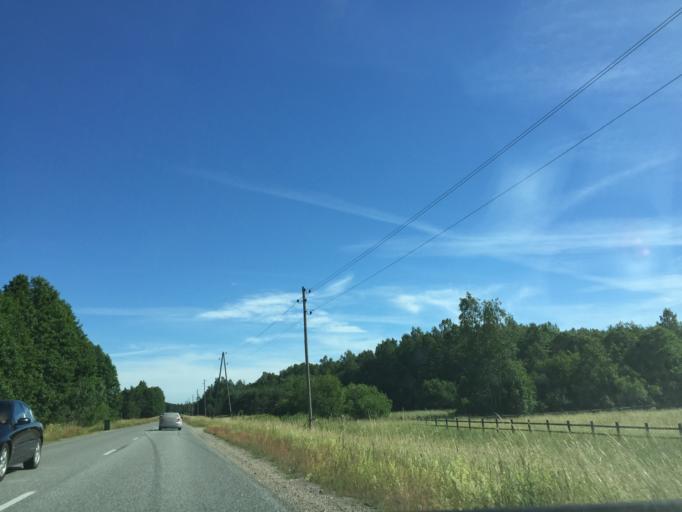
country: LV
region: Rojas
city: Roja
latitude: 57.4712
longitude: 22.8681
